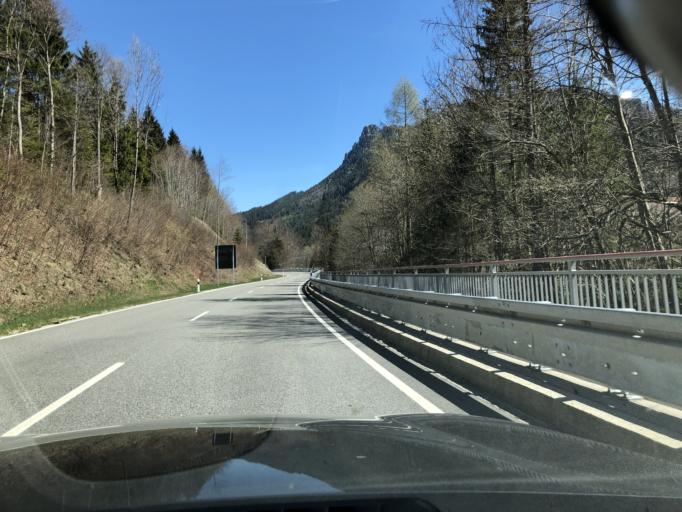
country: AT
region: Tyrol
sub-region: Politischer Bezirk Reutte
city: Jungholz
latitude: 47.5442
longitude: 10.4213
